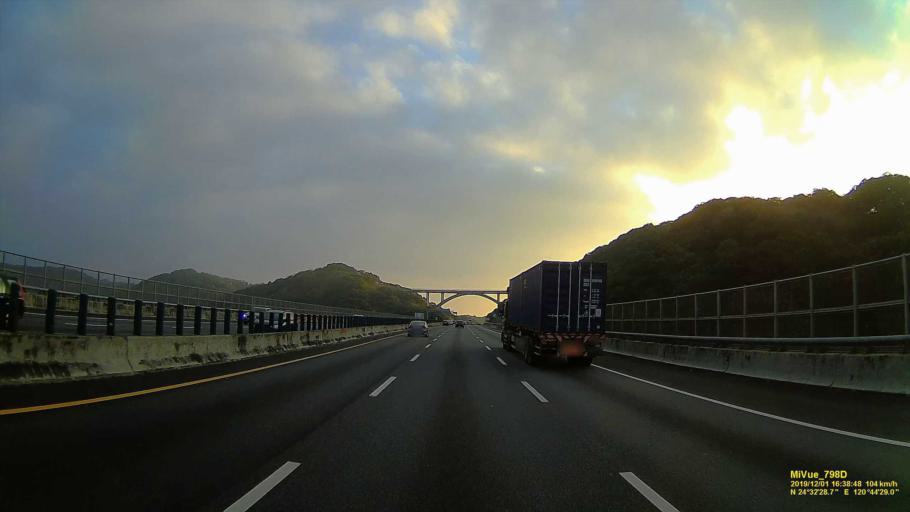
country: TW
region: Taiwan
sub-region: Miaoli
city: Miaoli
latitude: 24.5412
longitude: 120.7409
